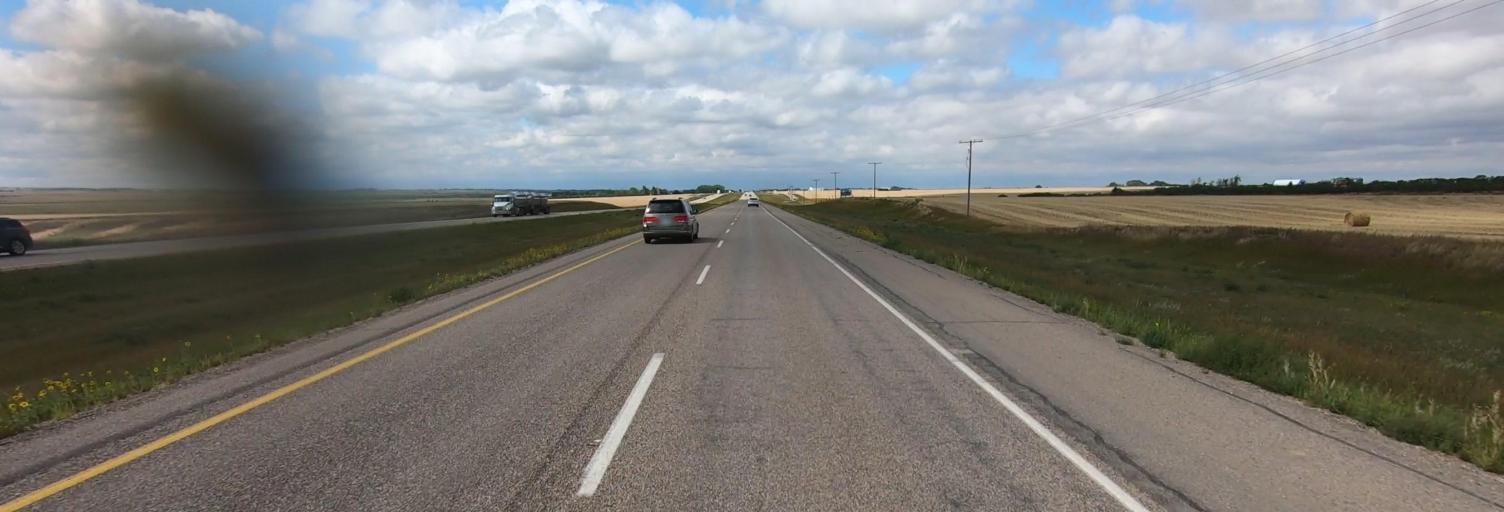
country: CA
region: Saskatchewan
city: Moose Jaw
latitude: 50.4360
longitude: -105.7603
